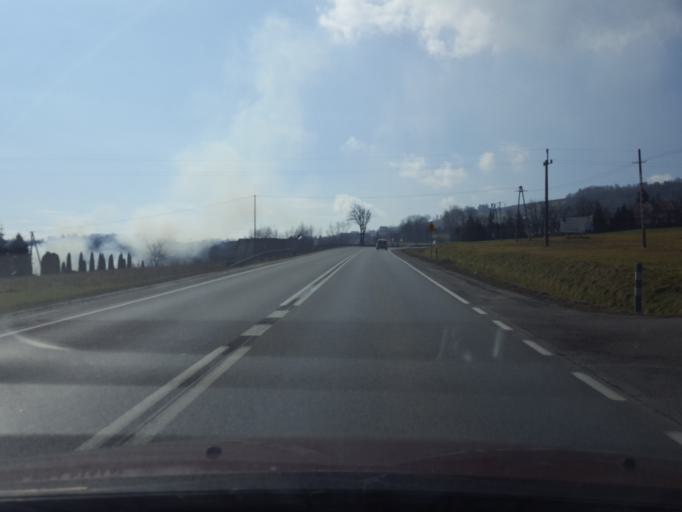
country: PL
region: Lesser Poland Voivodeship
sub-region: Powiat nowosadecki
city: Lososina Dolna
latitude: 49.7357
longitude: 20.6379
